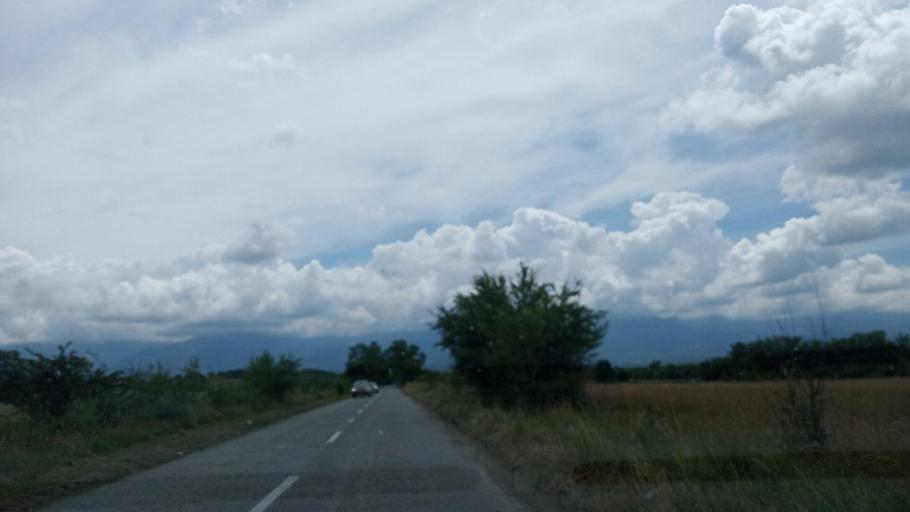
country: RO
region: Sibiu
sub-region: Comuna Porumbacu de Jos
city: Porumbacu de Jos
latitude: 45.7446
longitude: 24.4635
